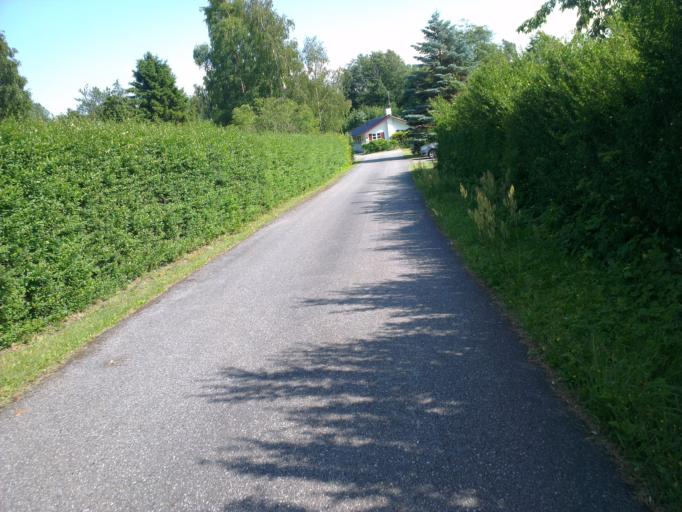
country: DK
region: Capital Region
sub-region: Halsnaes Kommune
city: Hundested
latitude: 55.9252
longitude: 11.9189
